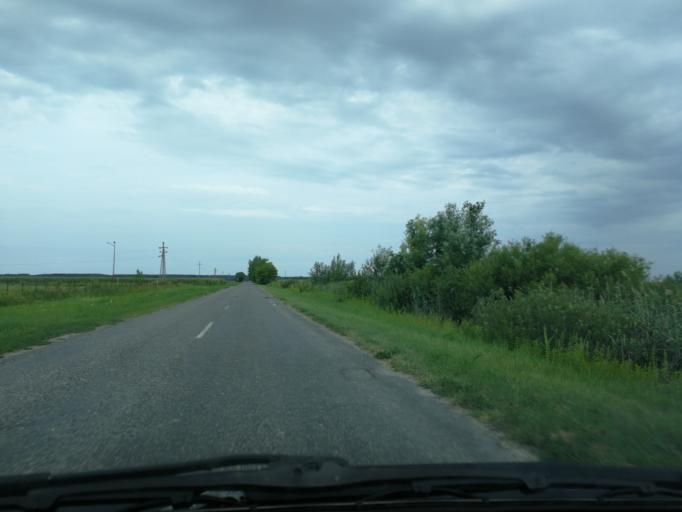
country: HU
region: Bacs-Kiskun
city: Batya
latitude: 46.4486
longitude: 18.9771
